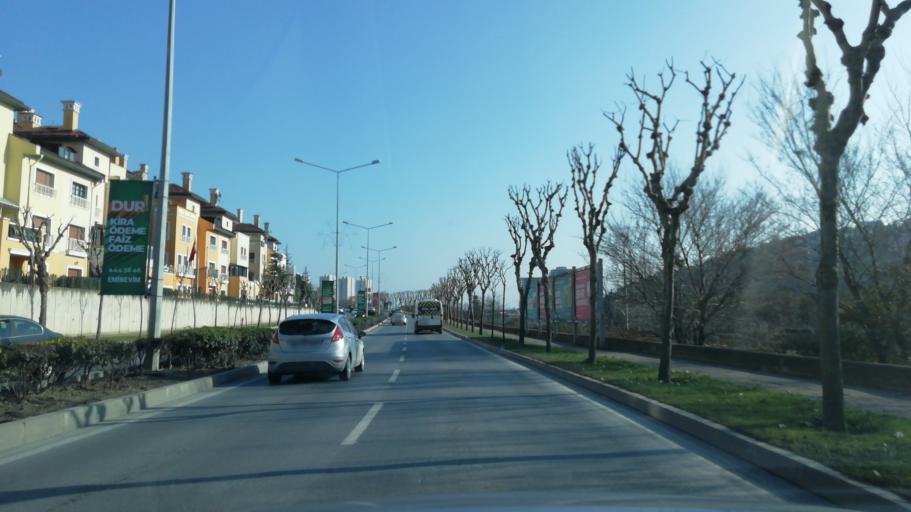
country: TR
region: Istanbul
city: Esenyurt
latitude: 41.0695
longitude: 28.6940
